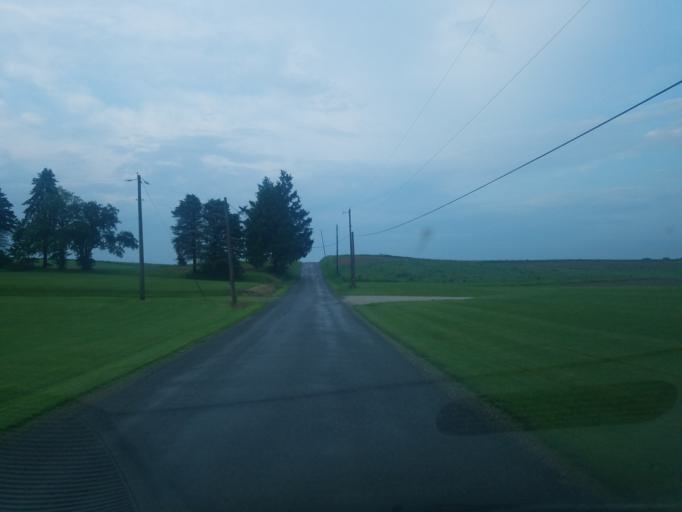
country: US
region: Ohio
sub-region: Mahoning County
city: Sebring
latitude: 40.7909
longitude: -80.9555
